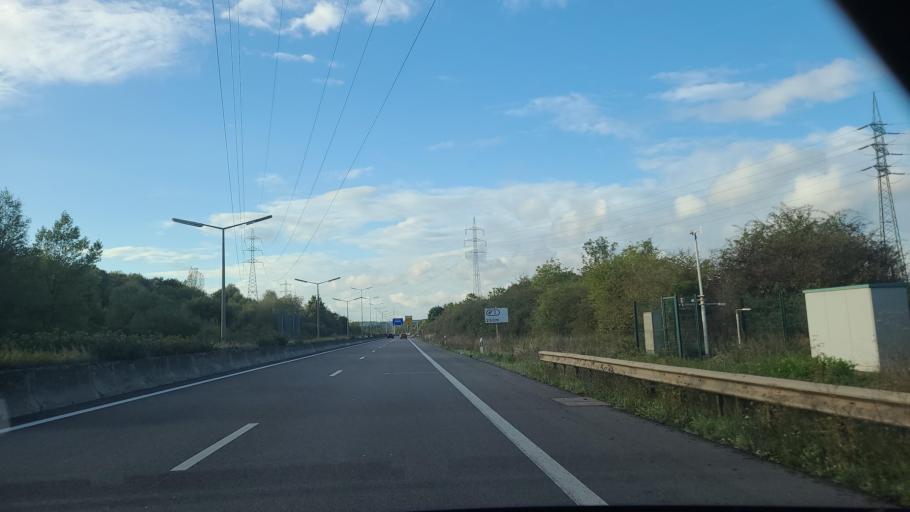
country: LU
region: Luxembourg
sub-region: Canton d'Esch-sur-Alzette
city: Sanem
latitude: 49.5382
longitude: 5.9241
